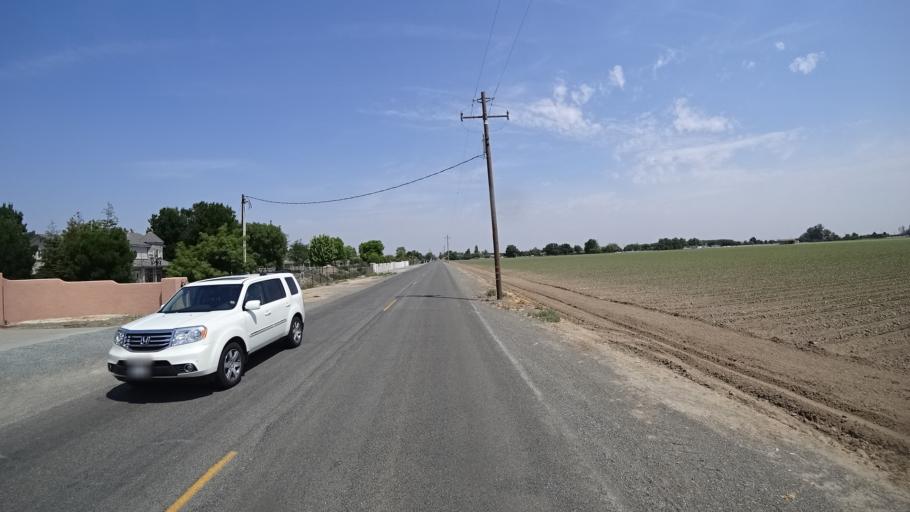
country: US
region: California
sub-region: Kings County
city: Lemoore
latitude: 36.3102
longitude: -119.7629
